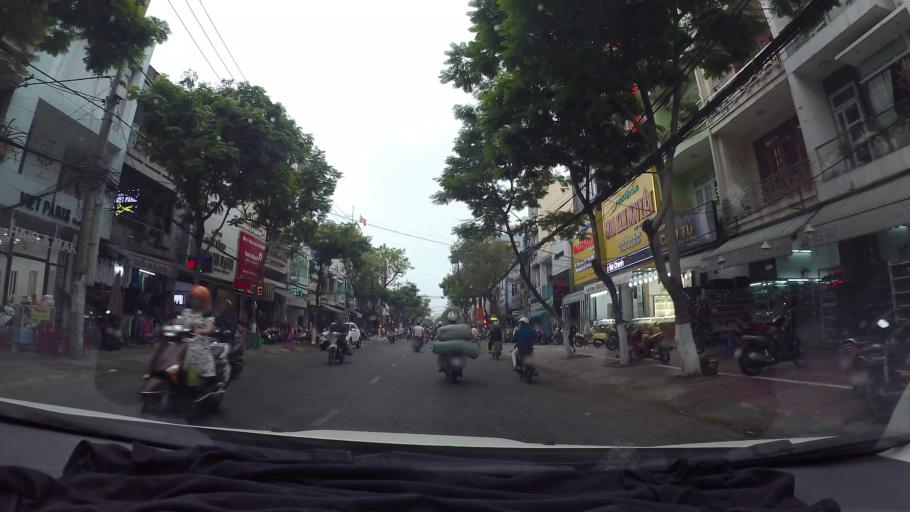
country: VN
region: Da Nang
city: Da Nang
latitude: 16.0695
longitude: 108.2136
